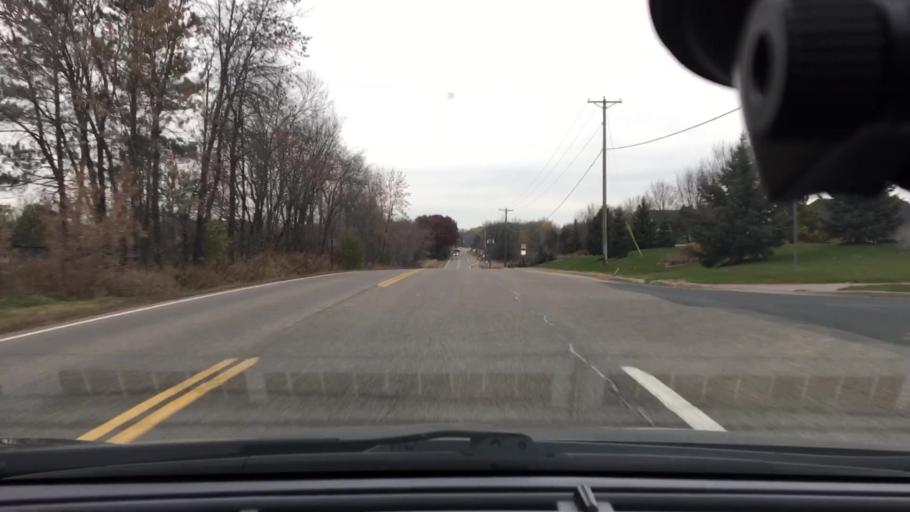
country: US
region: Minnesota
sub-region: Hennepin County
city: Corcoran
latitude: 45.0996
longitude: -93.5122
